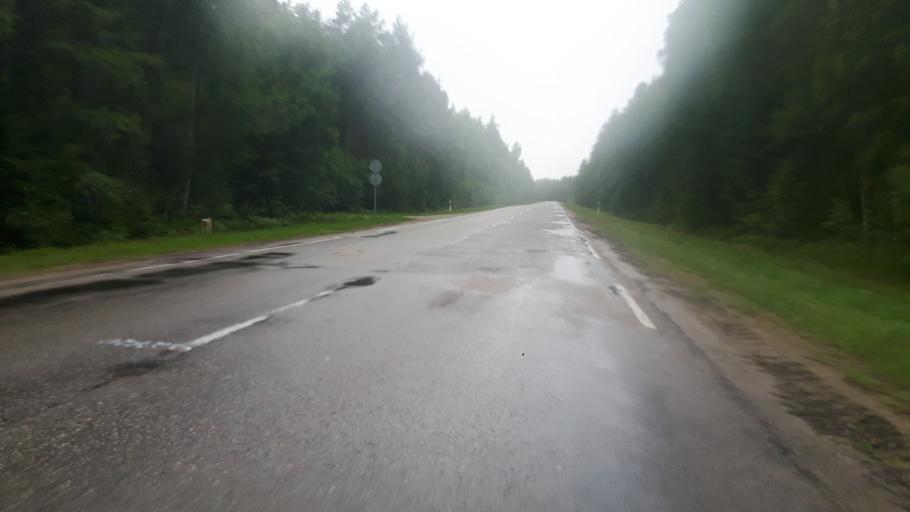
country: LV
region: Rucavas
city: Rucava
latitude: 56.1307
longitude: 21.1495
